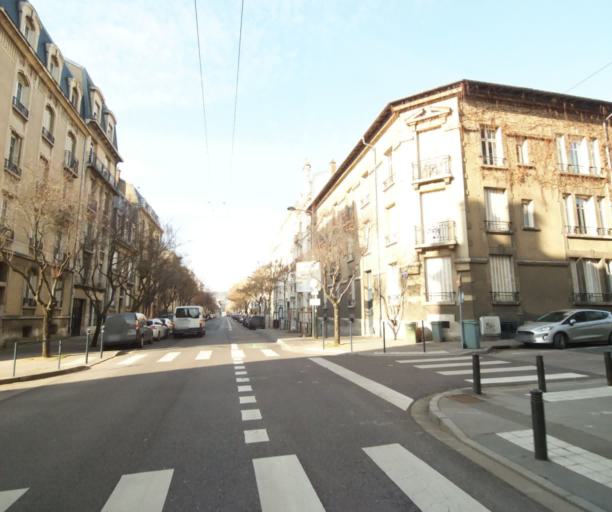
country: FR
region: Lorraine
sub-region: Departement de Meurthe-et-Moselle
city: Laxou
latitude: 48.6859
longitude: 6.1581
